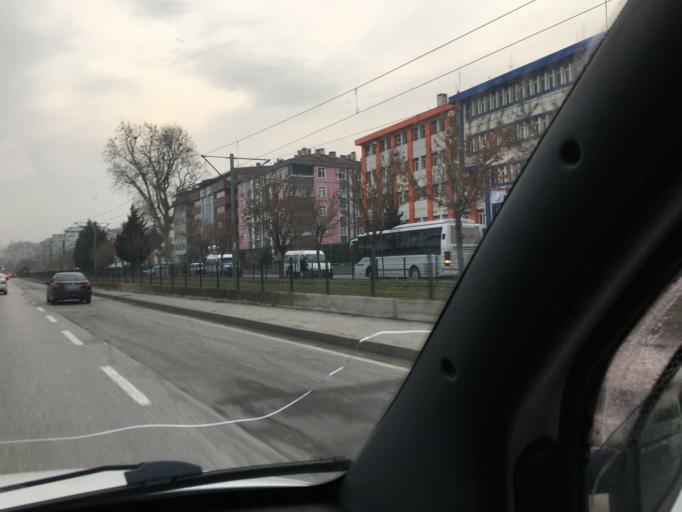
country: TR
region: Samsun
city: Samsun
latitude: 41.3087
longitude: 36.3345
